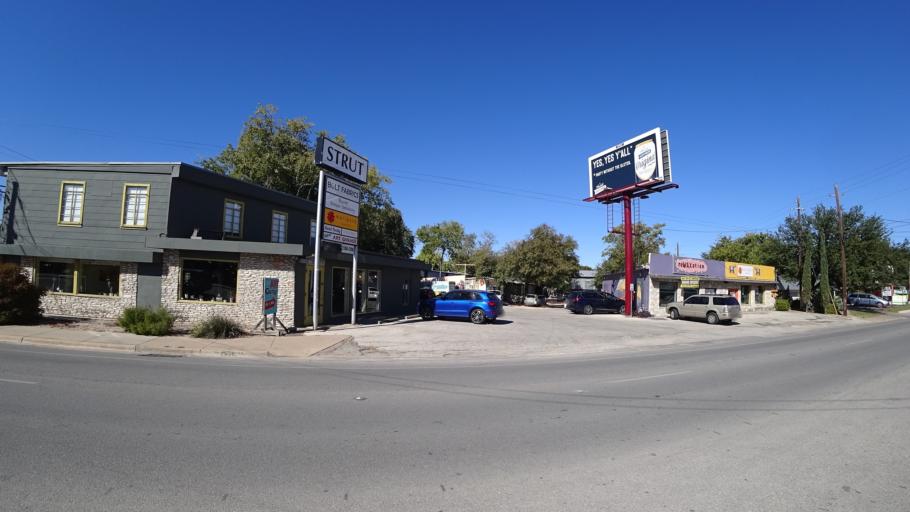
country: US
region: Texas
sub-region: Travis County
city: Rollingwood
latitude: 30.2476
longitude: -97.7729
